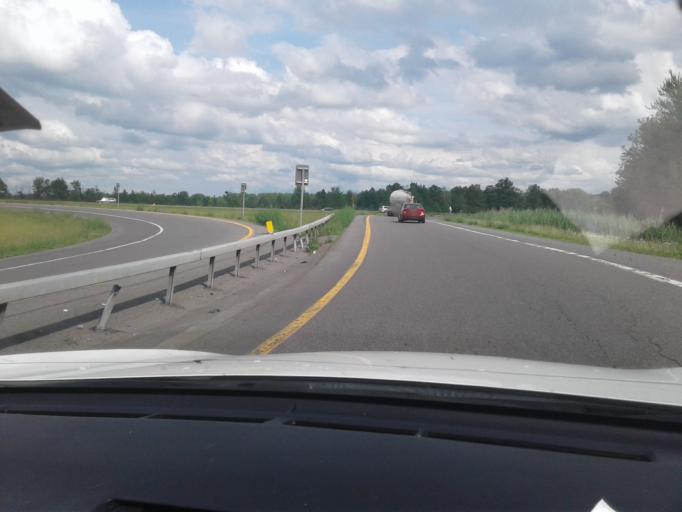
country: US
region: New York
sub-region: Onondaga County
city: East Syracuse
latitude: 43.0758
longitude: -76.0554
